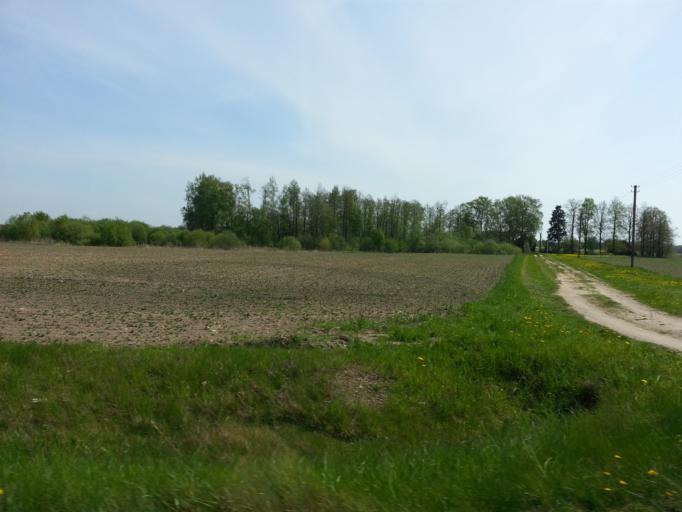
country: LT
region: Panevezys
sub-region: Panevezys City
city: Panevezys
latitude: 55.8528
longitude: 24.2446
